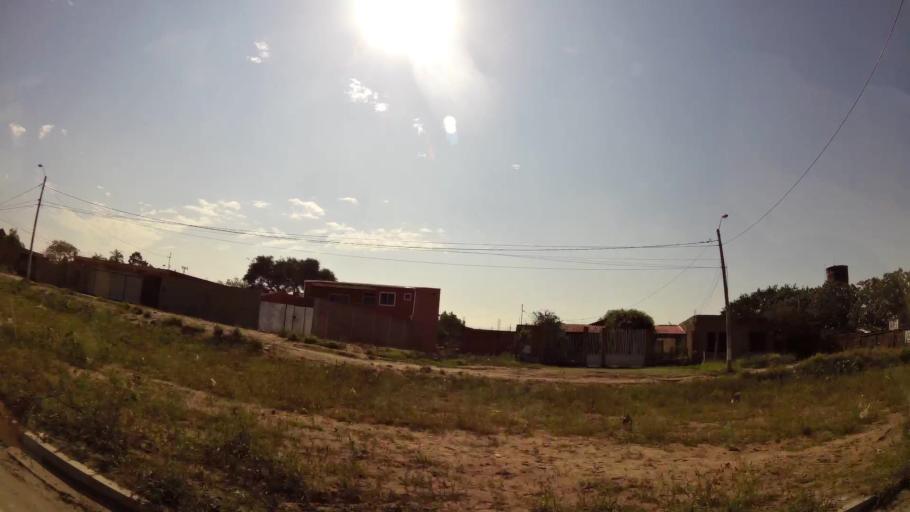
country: BO
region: Santa Cruz
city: Cotoca
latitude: -17.7564
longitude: -63.1050
